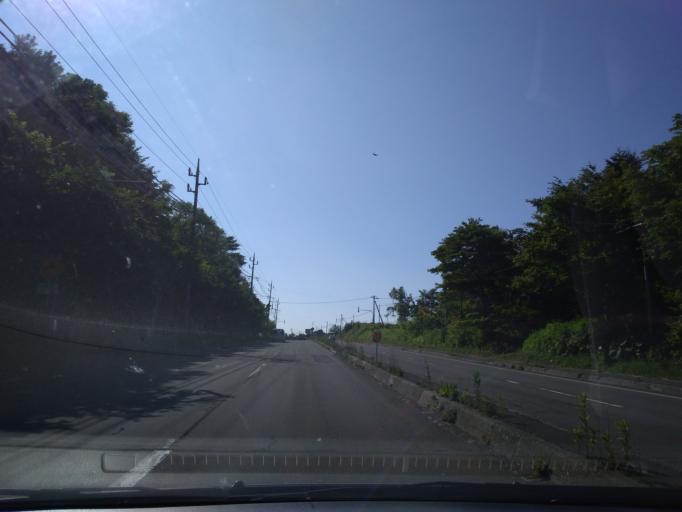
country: JP
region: Hokkaido
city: Kitahiroshima
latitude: 42.9793
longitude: 141.5042
